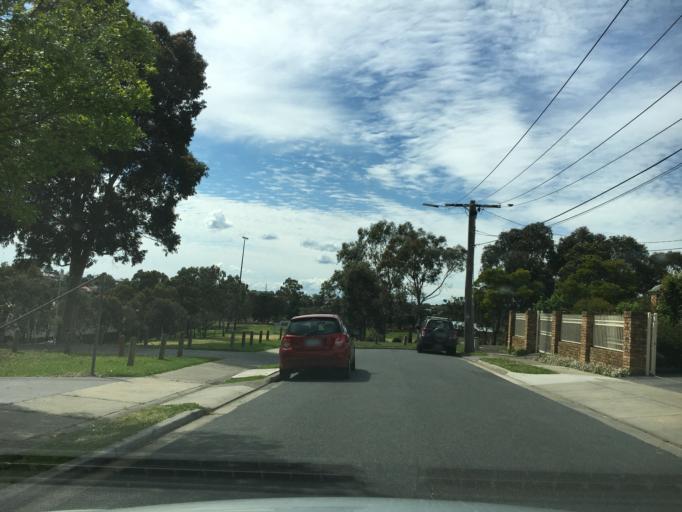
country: AU
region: Victoria
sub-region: Monash
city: Chadstone
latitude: -37.8949
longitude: 145.1023
